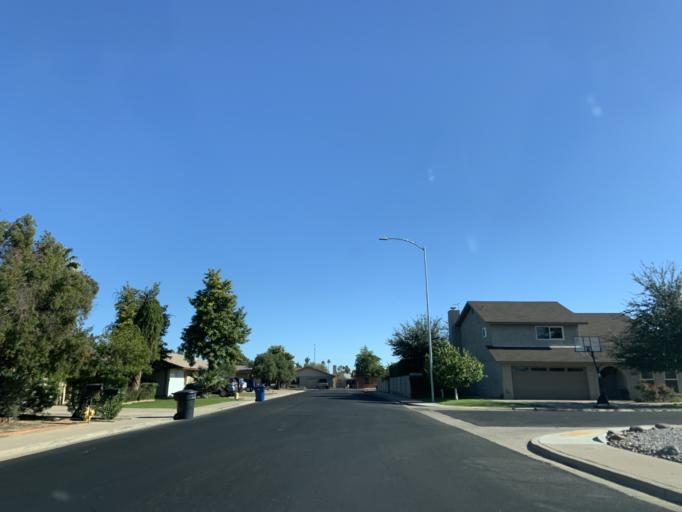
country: US
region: Arizona
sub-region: Maricopa County
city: San Carlos
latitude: 33.3753
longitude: -111.8614
